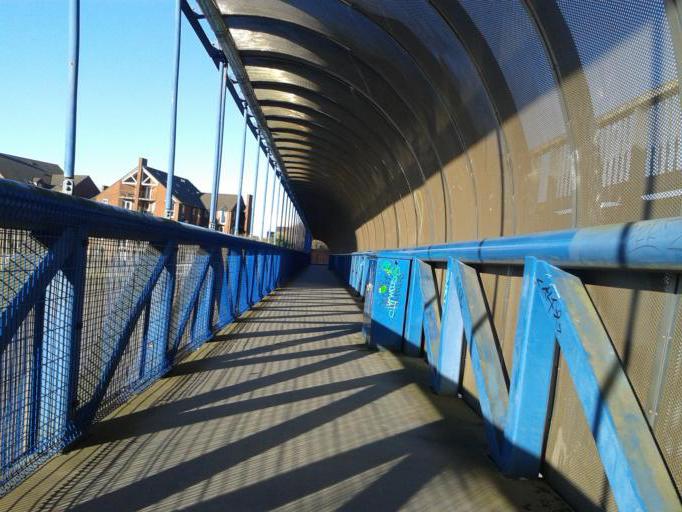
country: GB
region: Northern Ireland
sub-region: City of Belfast
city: Belfast
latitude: 54.5972
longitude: -5.9176
